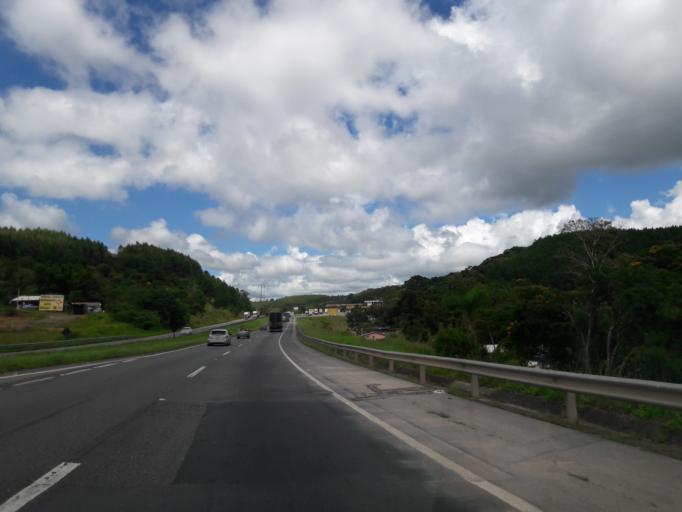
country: BR
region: Parana
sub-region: Campina Grande Do Sul
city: Campina Grande do Sul
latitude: -25.1172
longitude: -48.8541
